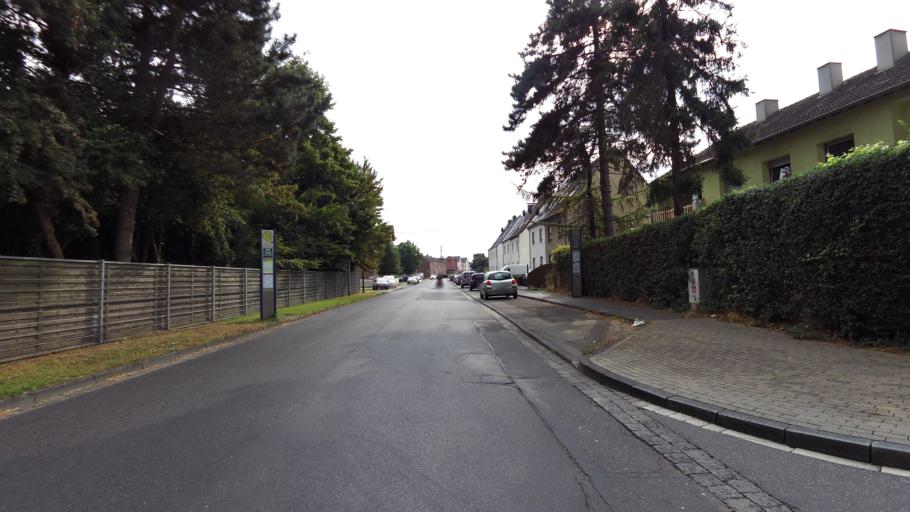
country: DE
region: North Rhine-Westphalia
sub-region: Regierungsbezirk Koln
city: Euskirchen
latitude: 50.6569
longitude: 6.8374
